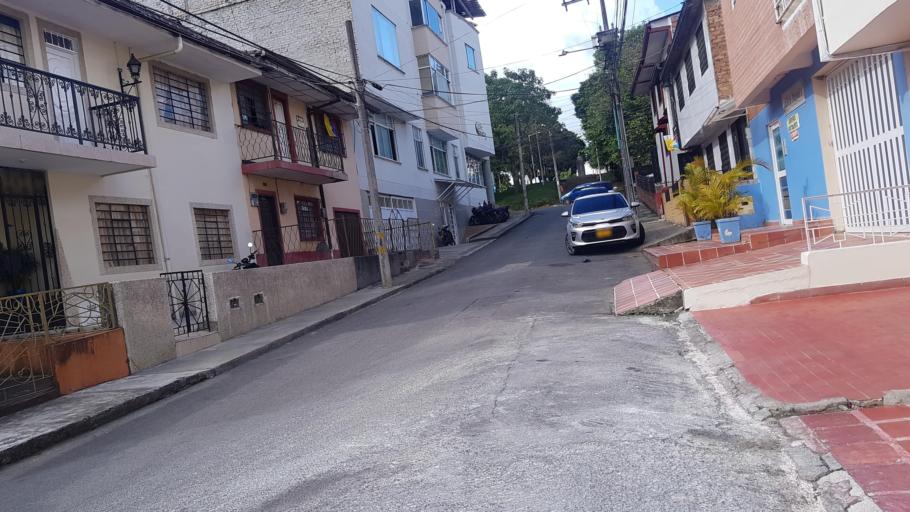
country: CO
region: Cauca
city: Popayan
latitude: 2.4394
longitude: -76.6126
